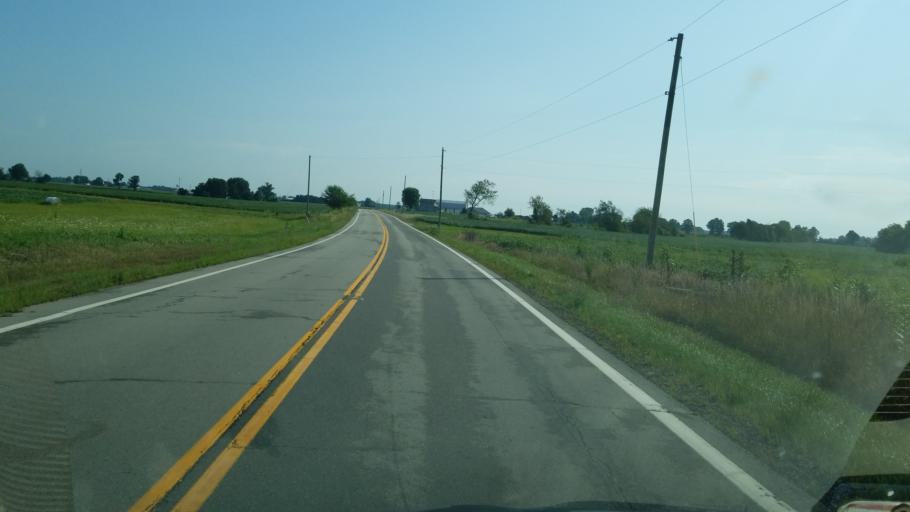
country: US
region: Ohio
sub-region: Crawford County
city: Crestline
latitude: 40.8427
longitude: -82.7115
